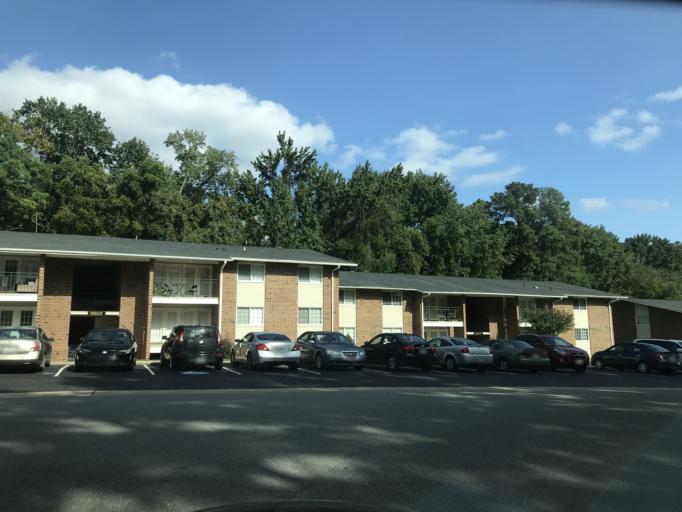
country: US
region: North Carolina
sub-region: Wake County
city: Raleigh
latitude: 35.8368
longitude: -78.5989
